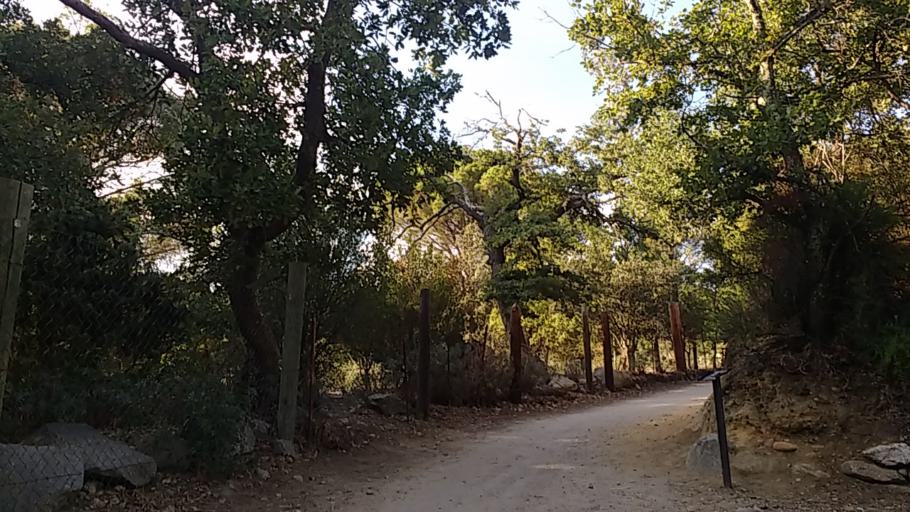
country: FR
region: Languedoc-Roussillon
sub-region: Departement des Pyrenees-Orientales
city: Ille-sur-Tet
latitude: 42.6842
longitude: 2.6197
